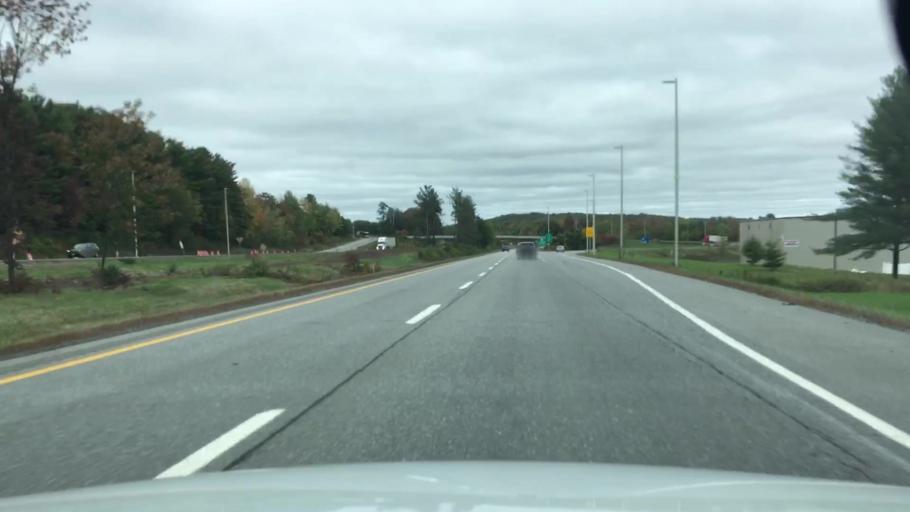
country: US
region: Maine
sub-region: Somerset County
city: Fairfield
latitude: 44.5904
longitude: -69.6186
